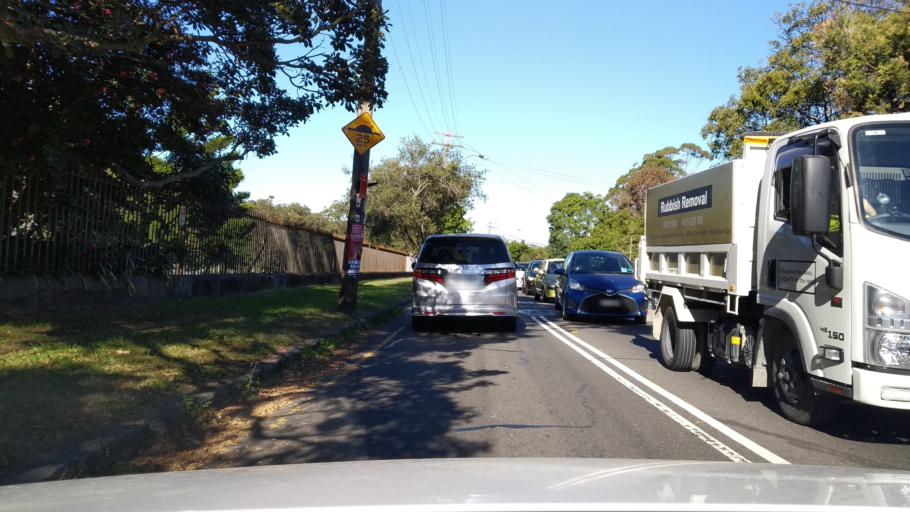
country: AU
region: New South Wales
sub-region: Woollahra
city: Woollahra
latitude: -33.8904
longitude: 151.2329
